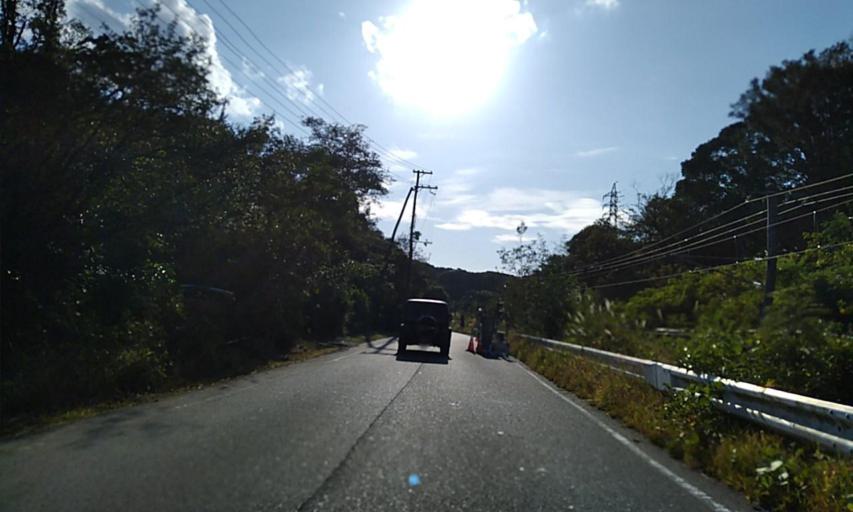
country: JP
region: Wakayama
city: Tanabe
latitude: 33.6827
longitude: 135.3990
